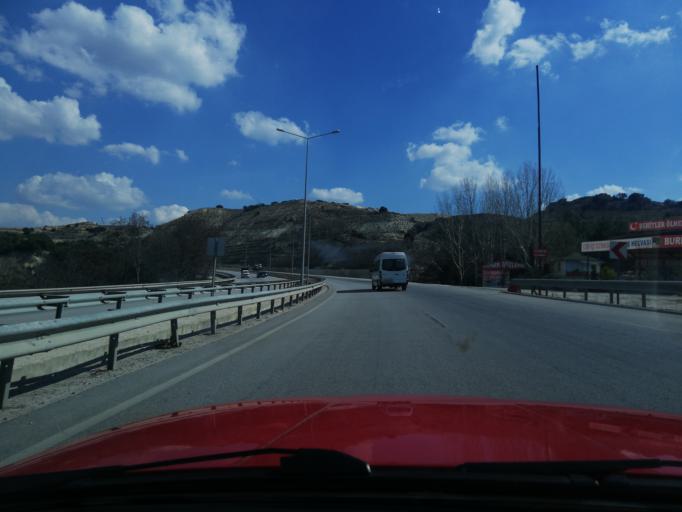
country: TR
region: Burdur
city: Burdur
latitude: 37.7027
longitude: 30.3072
